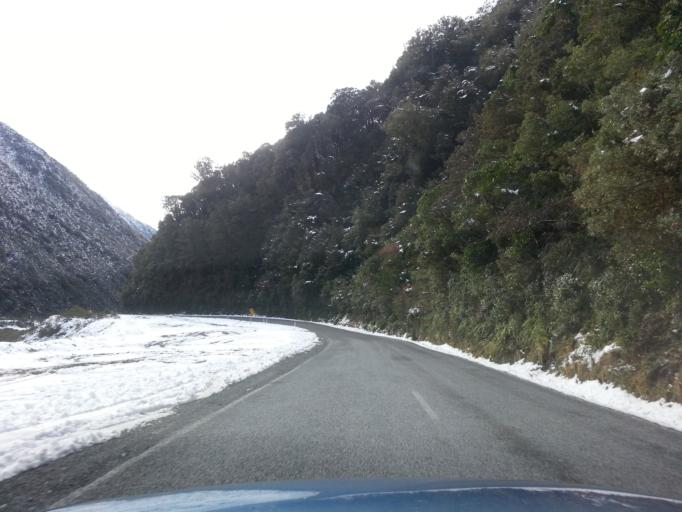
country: NZ
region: West Coast
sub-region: Grey District
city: Greymouth
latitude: -42.8579
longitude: 171.5597
